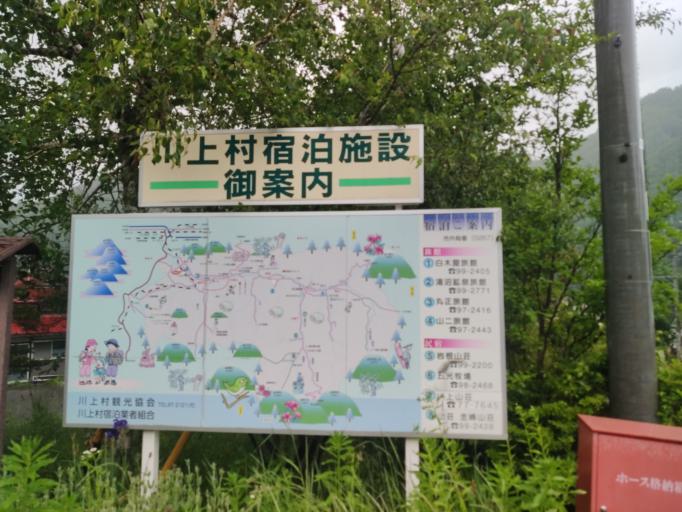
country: JP
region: Nagano
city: Saku
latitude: 35.9761
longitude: 138.5274
